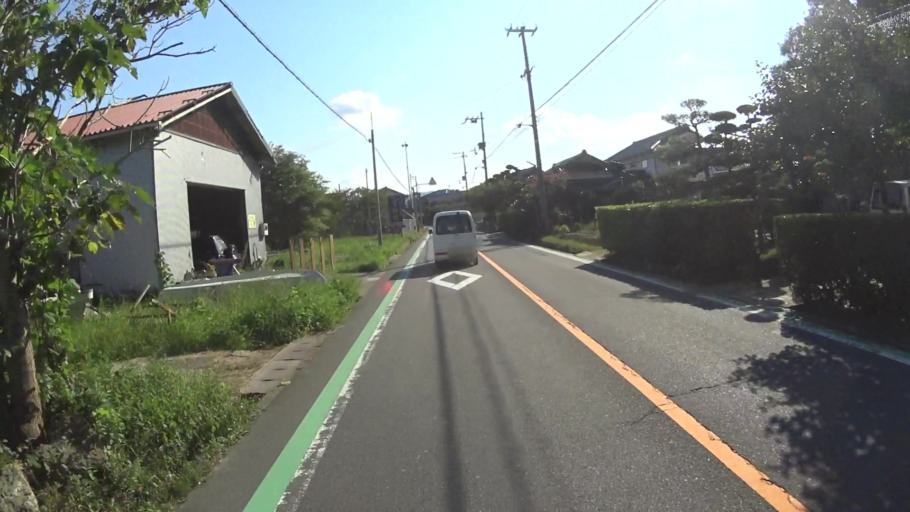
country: JP
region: Kyoto
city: Miyazu
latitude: 35.6923
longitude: 135.0358
